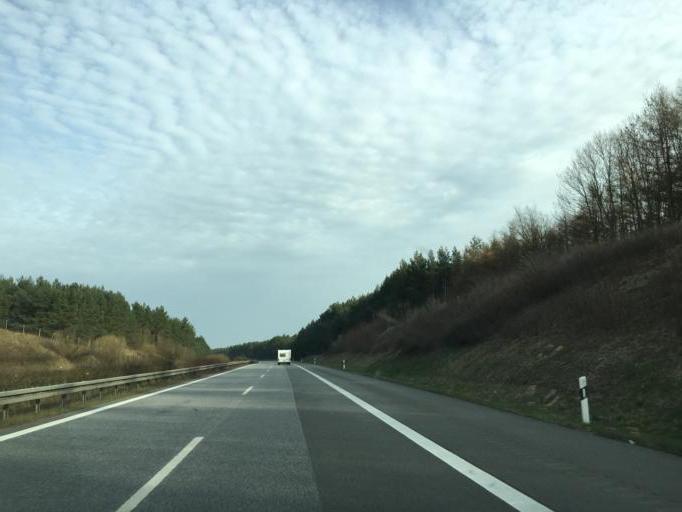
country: DE
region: Mecklenburg-Vorpommern
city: Malchow
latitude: 53.5257
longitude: 12.3540
